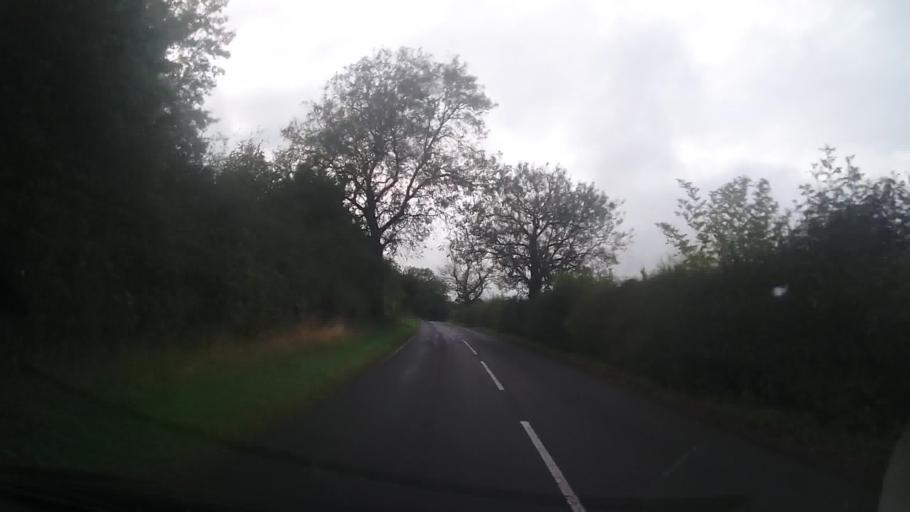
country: GB
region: England
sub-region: Oxfordshire
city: Chipping Norton
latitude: 51.9252
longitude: -1.5146
